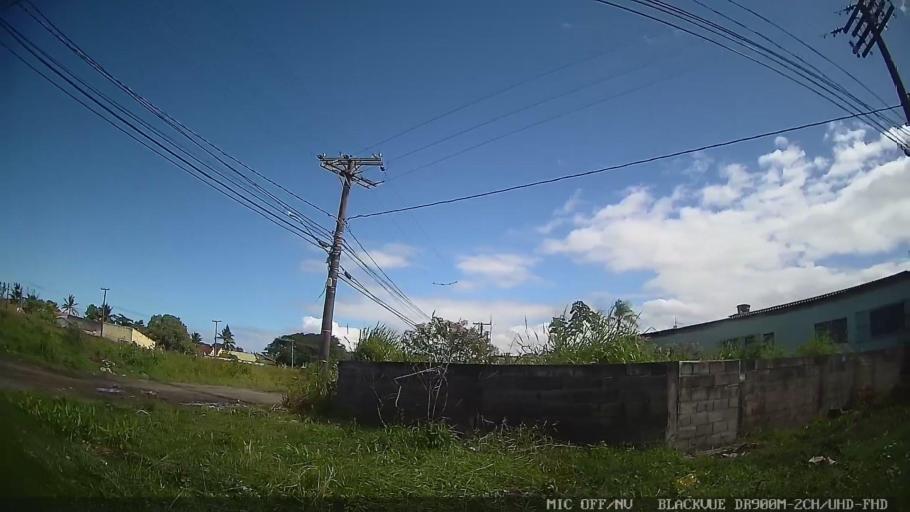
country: BR
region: Sao Paulo
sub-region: Itanhaem
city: Itanhaem
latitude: -24.2263
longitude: -46.8753
